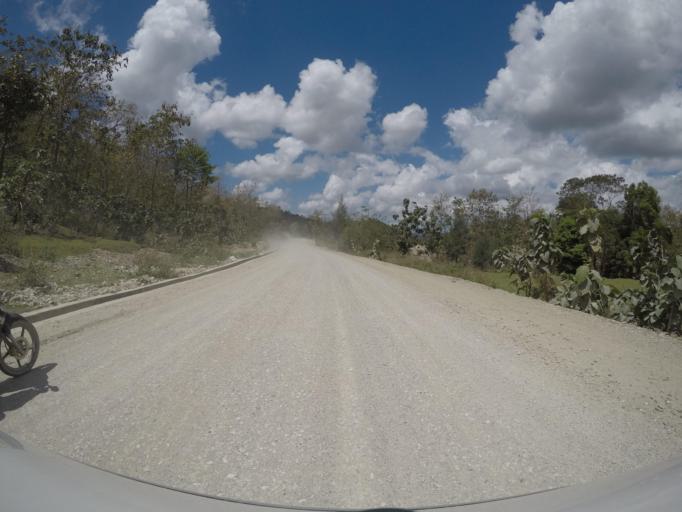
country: TL
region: Viqueque
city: Viqueque
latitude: -8.8190
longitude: 126.3787
